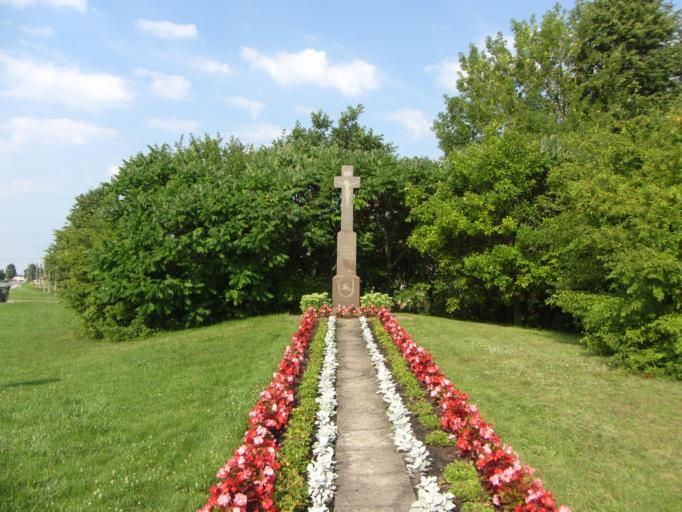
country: LT
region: Alytaus apskritis
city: Druskininkai
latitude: 54.0941
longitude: 23.8708
